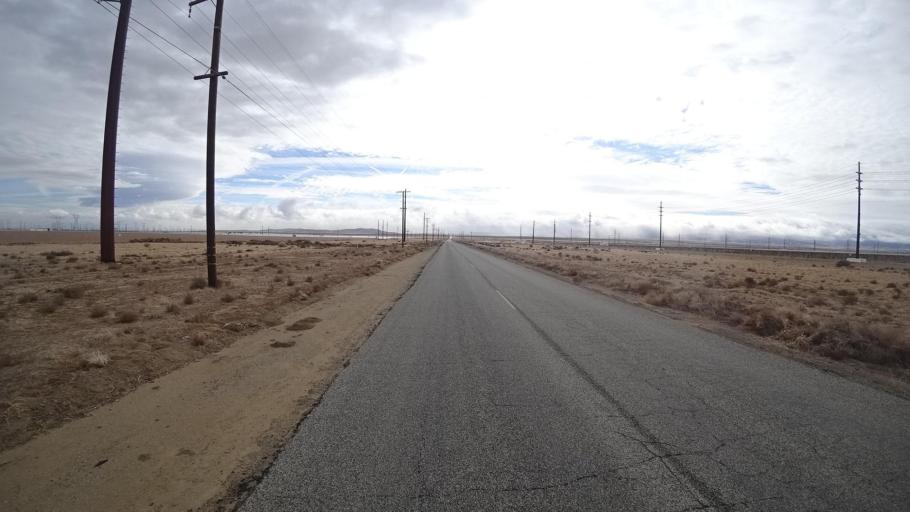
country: US
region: California
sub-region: Los Angeles County
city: Green Valley
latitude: 34.8349
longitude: -118.4324
